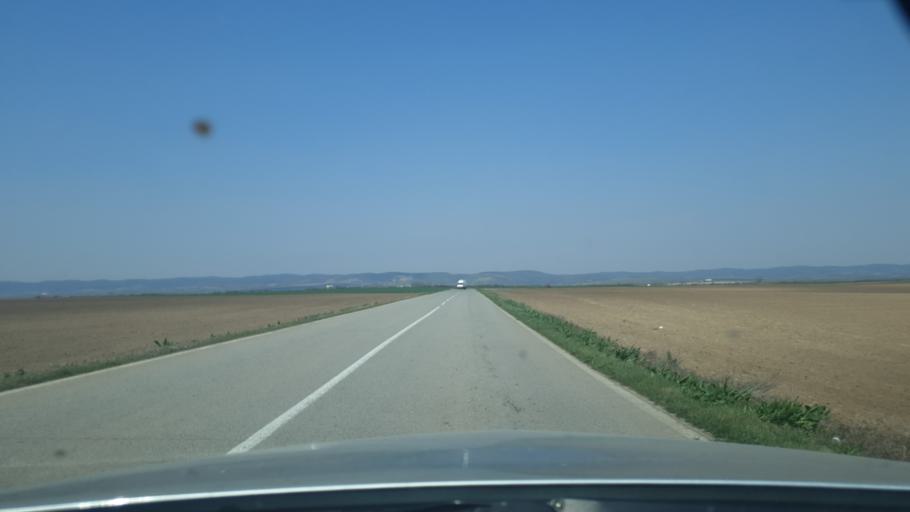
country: RS
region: Autonomna Pokrajina Vojvodina
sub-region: Sremski Okrug
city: Ruma
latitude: 45.0418
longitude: 19.7608
